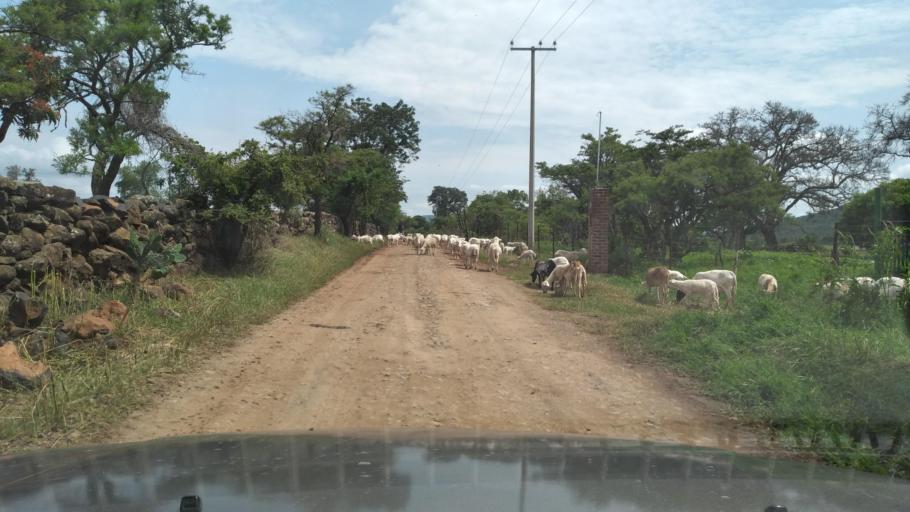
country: MX
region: Jalisco
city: Capilla de Guadalupe
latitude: 20.7461
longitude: -102.6324
